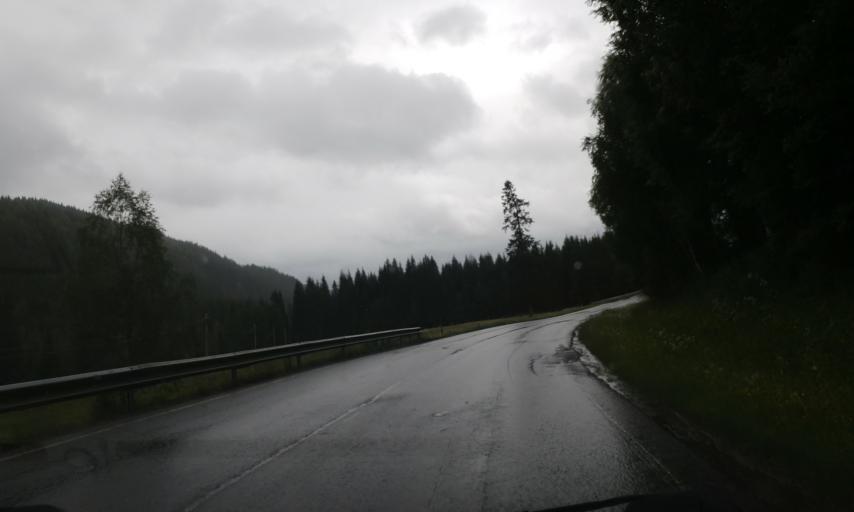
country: NO
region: Sor-Trondelag
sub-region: Selbu
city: Mebonden
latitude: 63.2950
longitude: 11.0770
